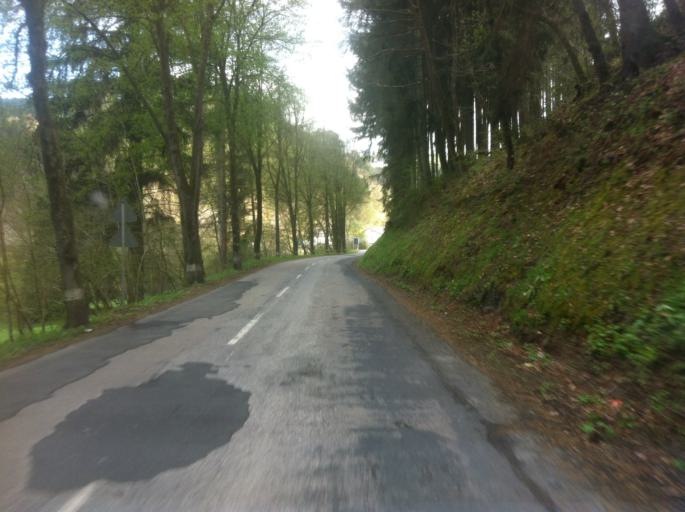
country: DE
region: Rheinland-Pfalz
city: Dasburg
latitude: 50.0512
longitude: 6.1225
